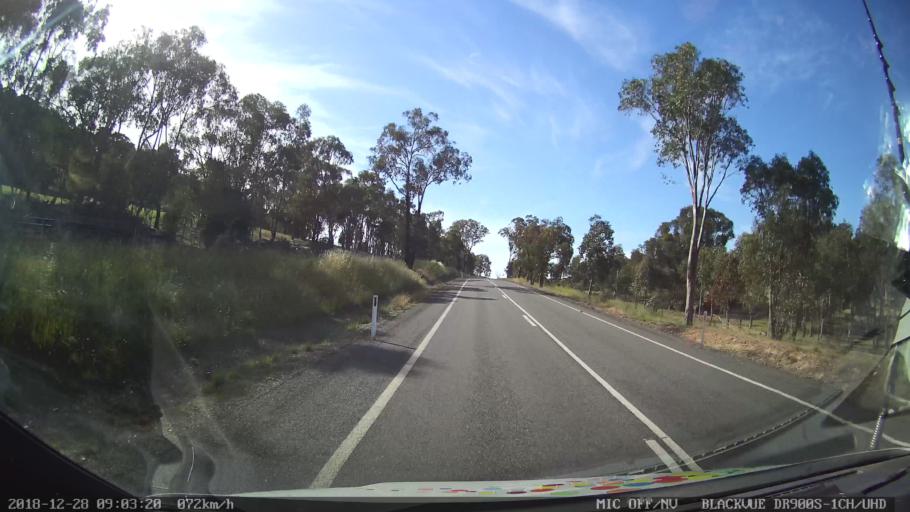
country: AU
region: New South Wales
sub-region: Upper Lachlan Shire
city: Crookwell
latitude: -34.1625
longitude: 149.3368
